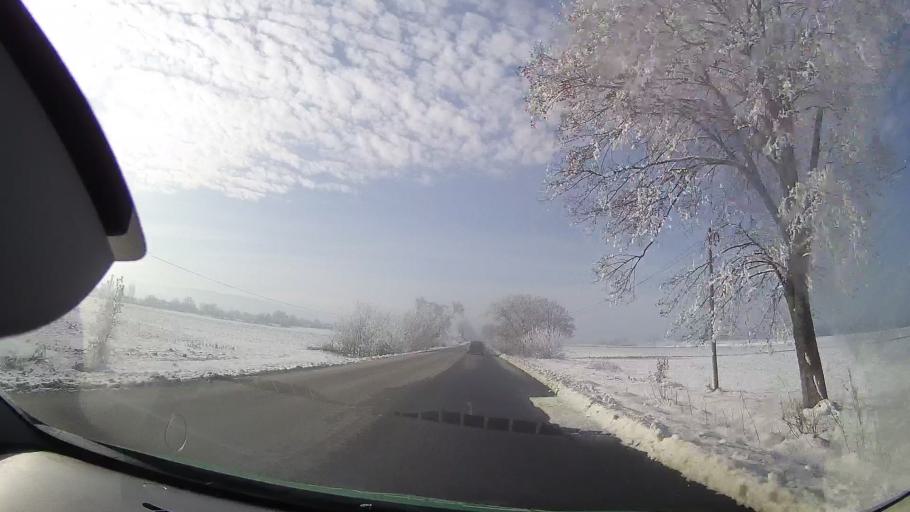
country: RO
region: Neamt
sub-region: Comuna Timisesti
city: Dumbrava
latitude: 47.2242
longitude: 26.4807
